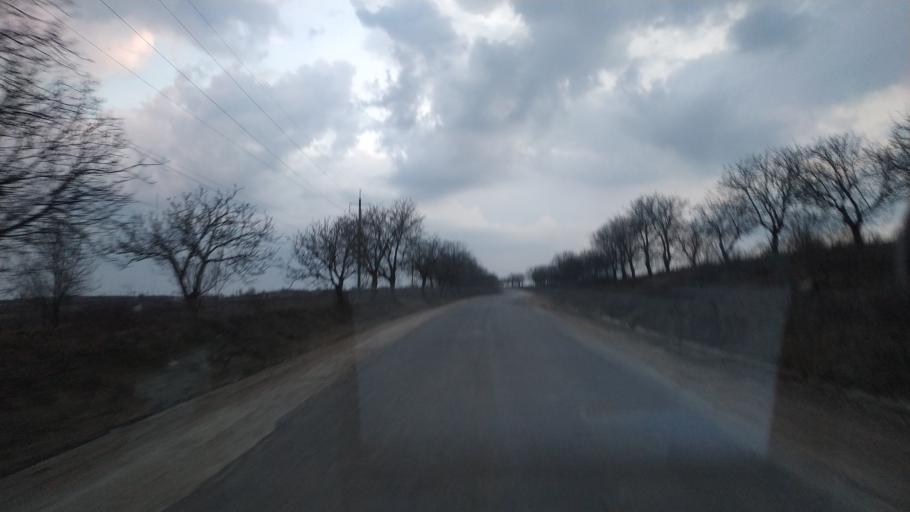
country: MD
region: Anenii Noi
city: Anenii Noi
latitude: 46.9702
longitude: 29.2852
